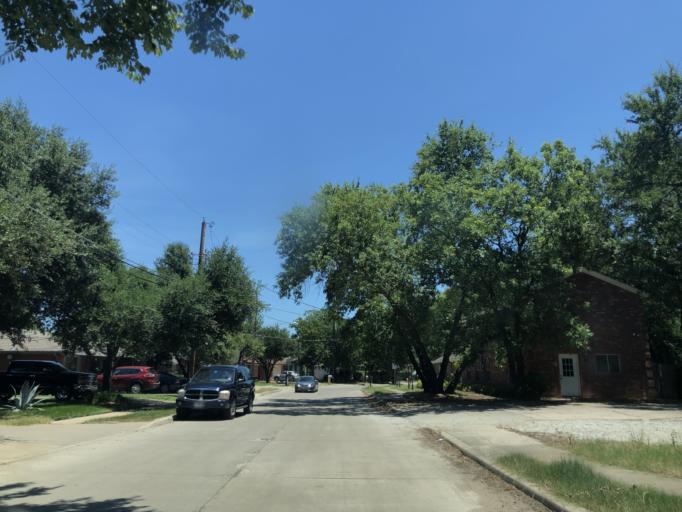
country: US
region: Texas
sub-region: Dallas County
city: Irving
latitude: 32.7951
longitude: -96.8980
